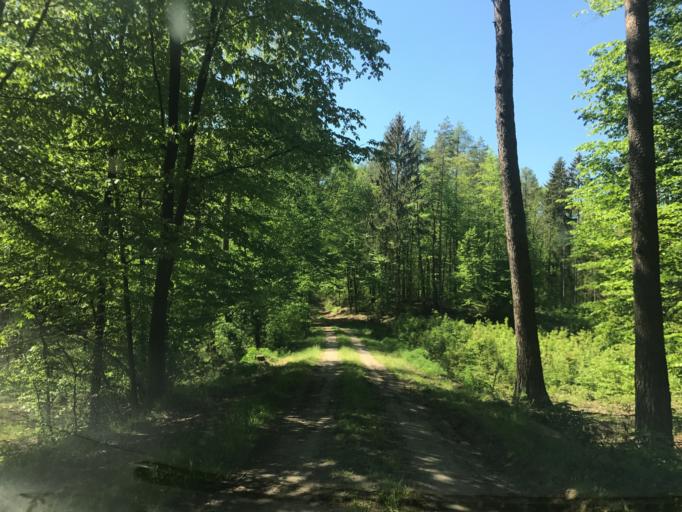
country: PL
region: Kujawsko-Pomorskie
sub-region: Powiat brodnicki
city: Gorzno
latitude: 53.2123
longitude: 19.7186
